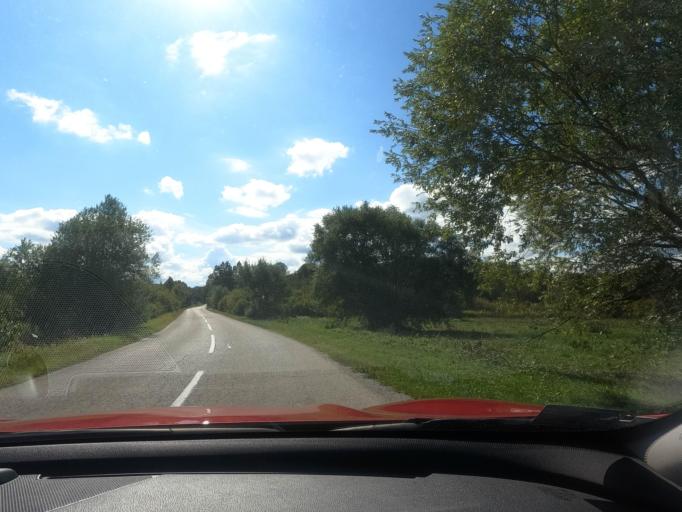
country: BA
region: Federation of Bosnia and Herzegovina
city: Vrnograc
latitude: 45.2477
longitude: 15.9416
